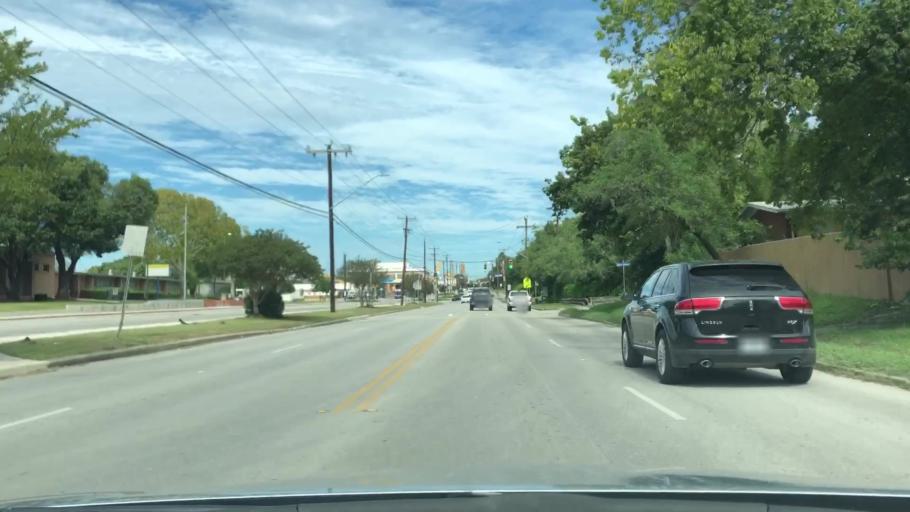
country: US
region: Texas
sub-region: Bexar County
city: Castle Hills
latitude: 29.5119
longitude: -98.4917
